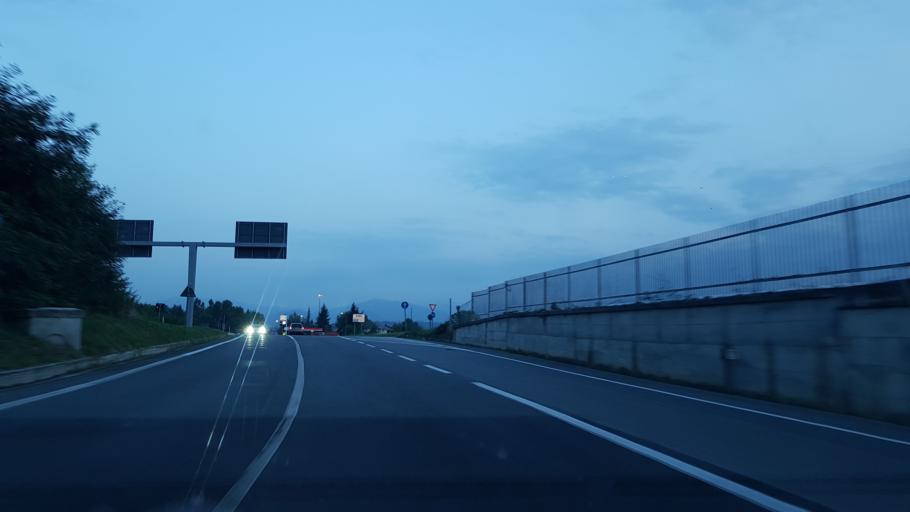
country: IT
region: Piedmont
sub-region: Provincia di Cuneo
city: Breo
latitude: 44.4133
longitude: 7.8009
